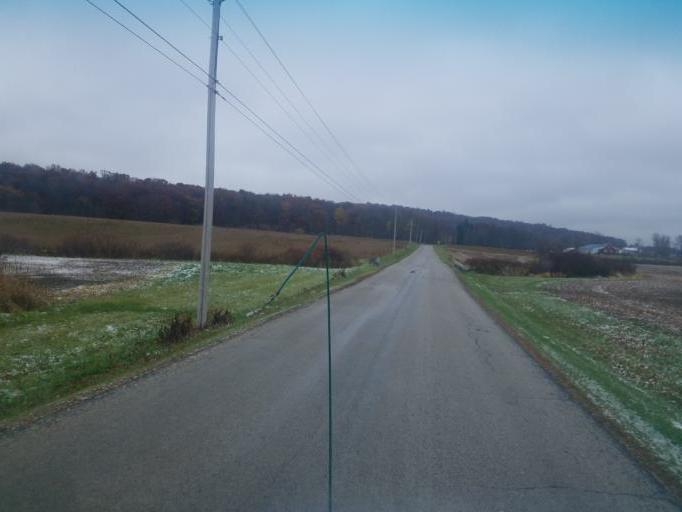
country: US
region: Ohio
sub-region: Richland County
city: Lincoln Heights
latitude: 40.8293
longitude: -82.4626
